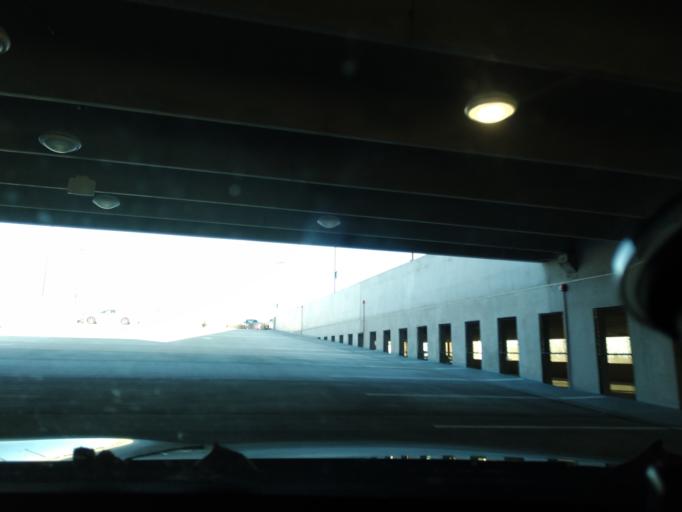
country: US
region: Maryland
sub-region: Calvert County
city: Chesapeake Beach
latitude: 38.6904
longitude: -76.5352
